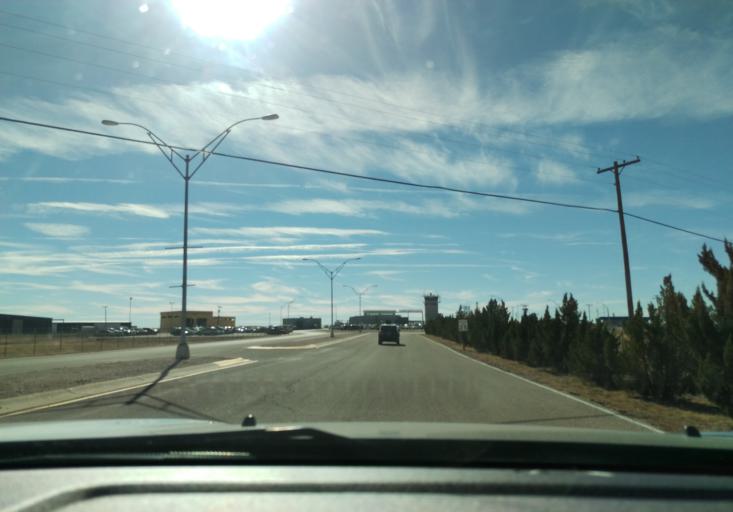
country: US
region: New Mexico
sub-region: Lea County
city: Hobbs
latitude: 32.6951
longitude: -103.2144
